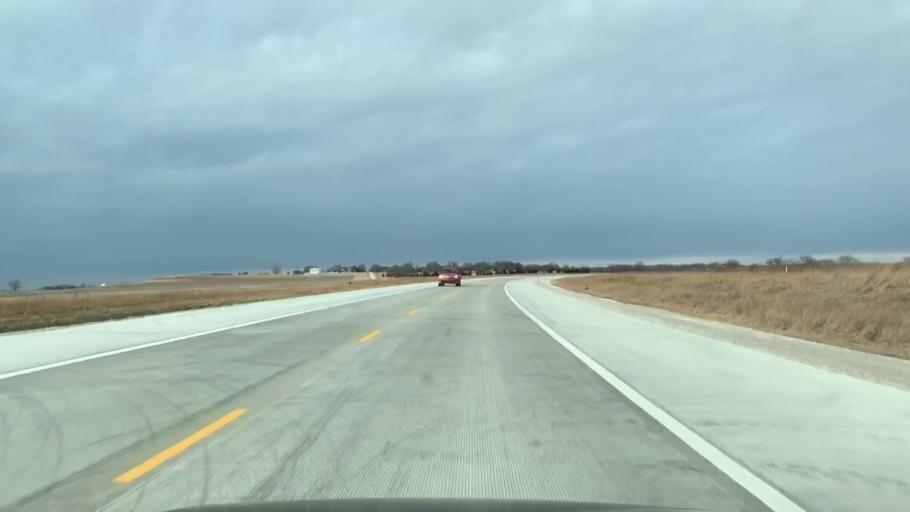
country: US
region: Kansas
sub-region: Allen County
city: Humboldt
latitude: 37.8521
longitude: -95.4096
